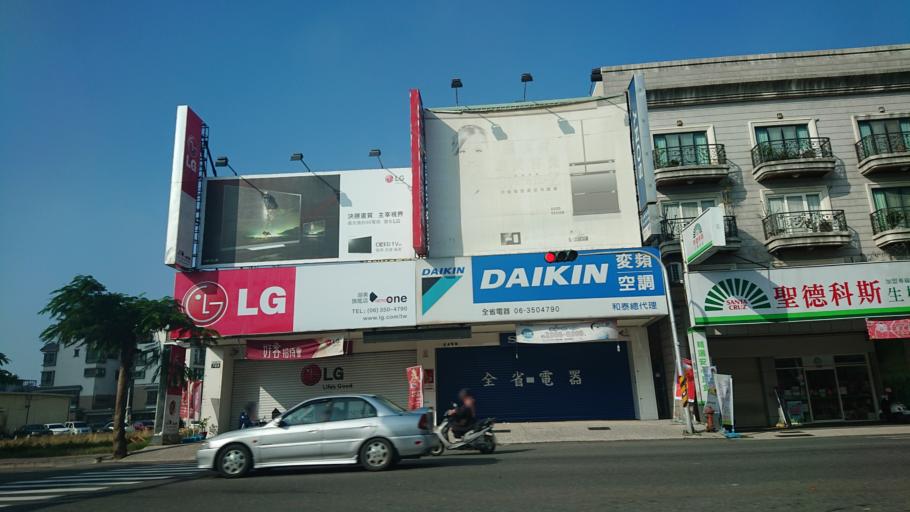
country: TW
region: Taiwan
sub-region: Tainan
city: Tainan
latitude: 23.0042
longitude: 120.1869
